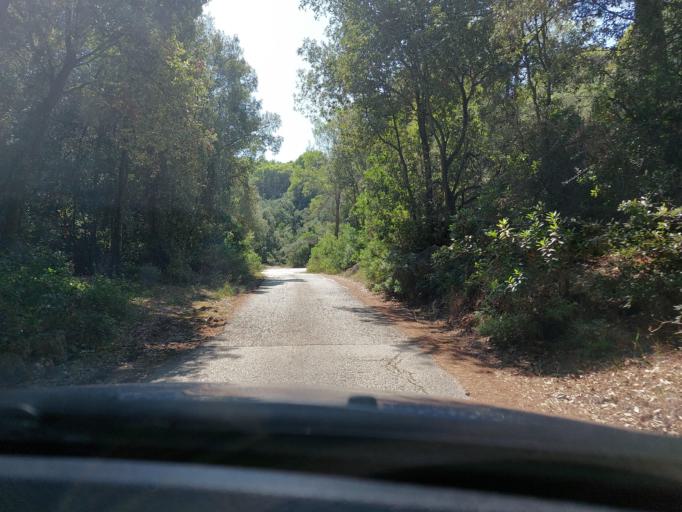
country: HR
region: Dubrovacko-Neretvanska
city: Smokvica
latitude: 42.7415
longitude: 16.8252
